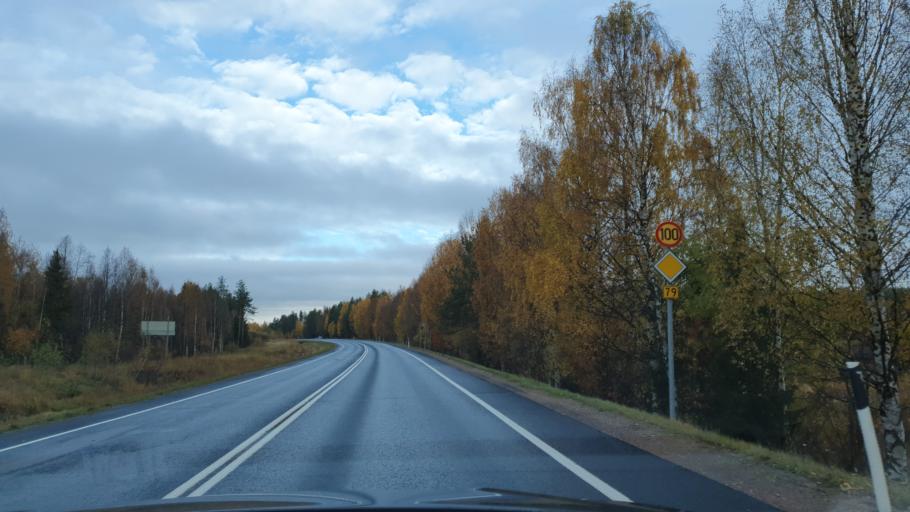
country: FI
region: Lapland
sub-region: Rovaniemi
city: Rovaniemi
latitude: 66.5979
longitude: 25.5942
